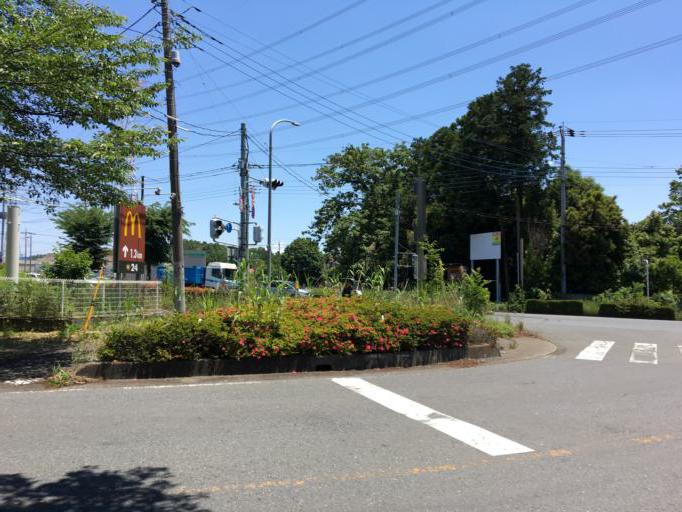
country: JP
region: Saitama
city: Sakado
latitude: 35.9319
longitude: 139.3855
